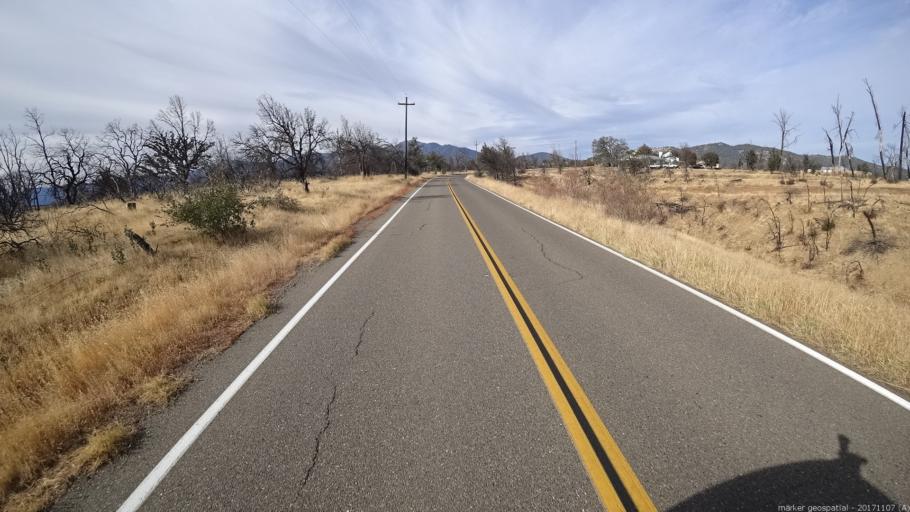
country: US
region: California
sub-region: Shasta County
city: Shasta
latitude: 40.4857
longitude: -122.5116
